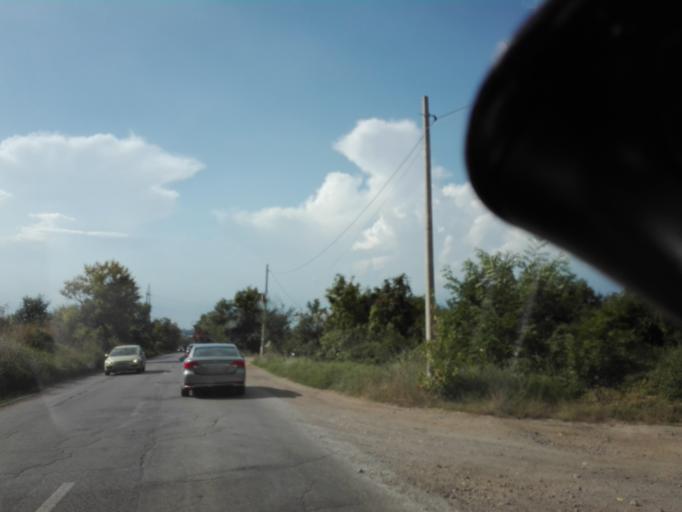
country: BG
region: Sofiya
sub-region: Obshtina Elin Pelin
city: Elin Pelin
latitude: 42.6161
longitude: 23.4583
